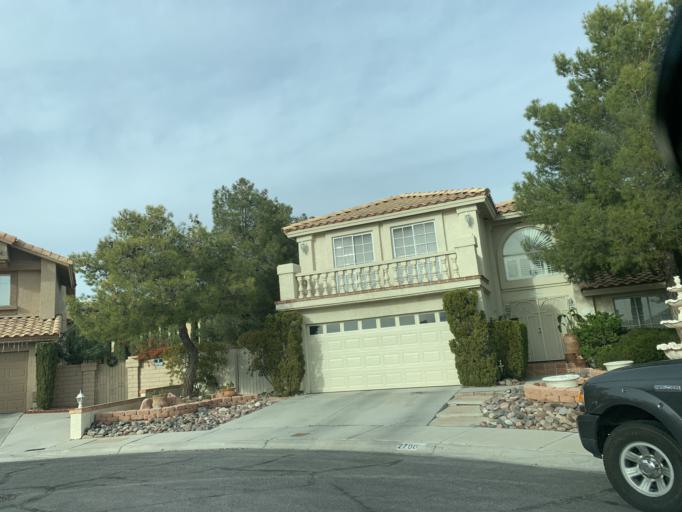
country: US
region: Nevada
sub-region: Clark County
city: Summerlin South
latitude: 36.1424
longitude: -115.3008
